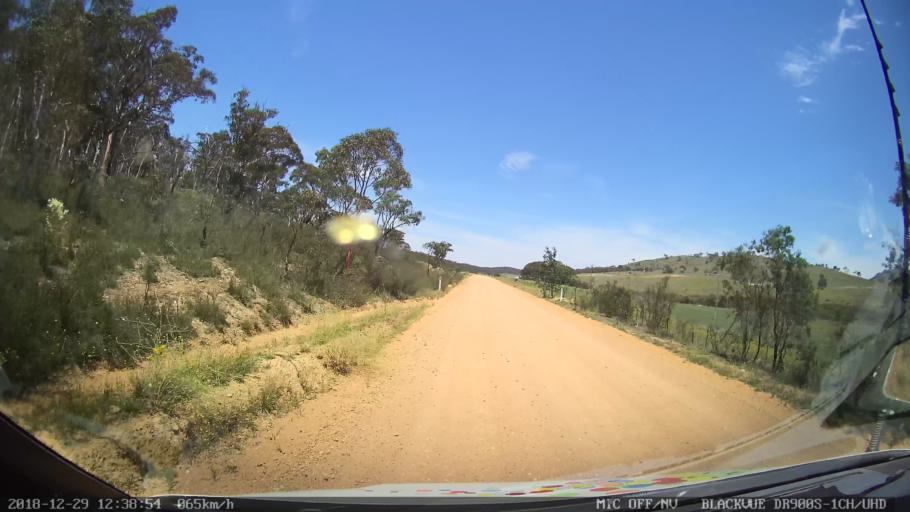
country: AU
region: Australian Capital Territory
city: Macarthur
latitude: -35.5929
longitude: 149.2282
